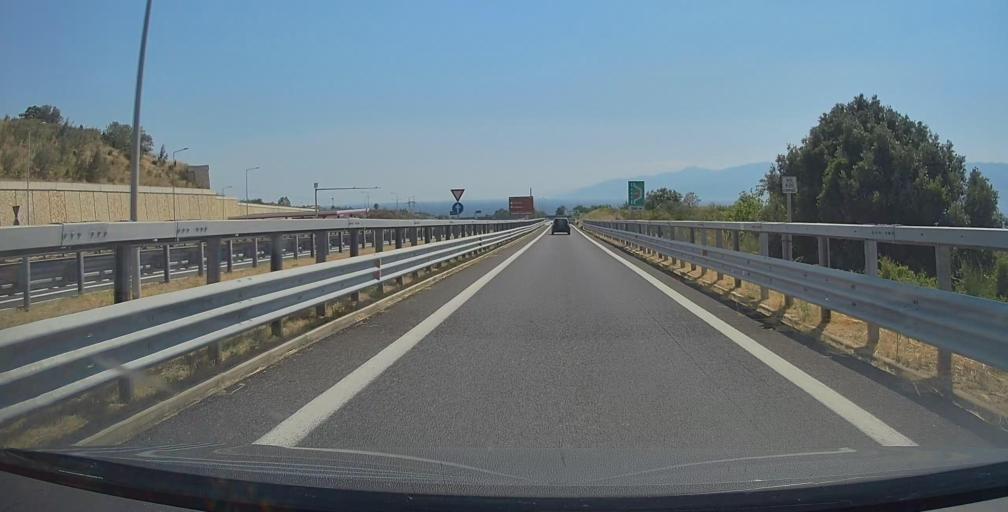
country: IT
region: Calabria
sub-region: Provincia di Reggio Calabria
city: Campo Calabro
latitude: 38.2110
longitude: 15.6448
